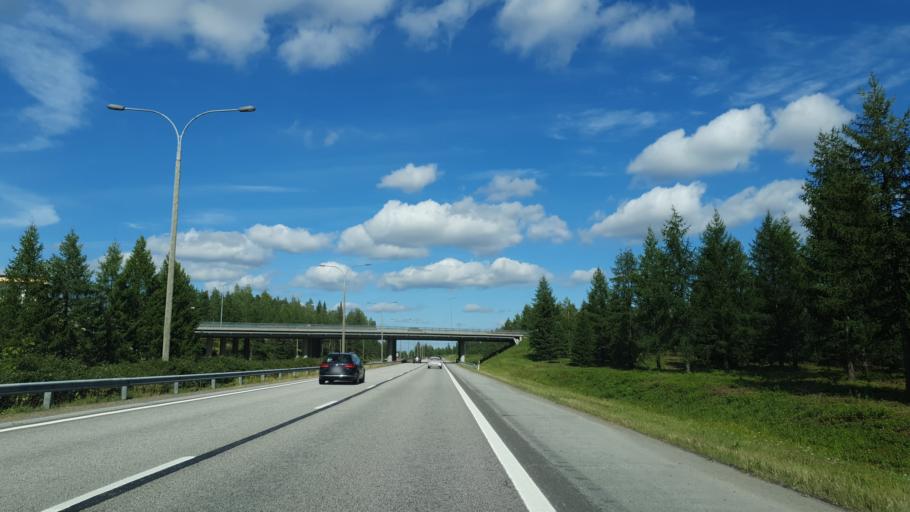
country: FI
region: Central Finland
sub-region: Jyvaeskylae
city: Jyvaeskylae
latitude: 62.1891
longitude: 25.6961
